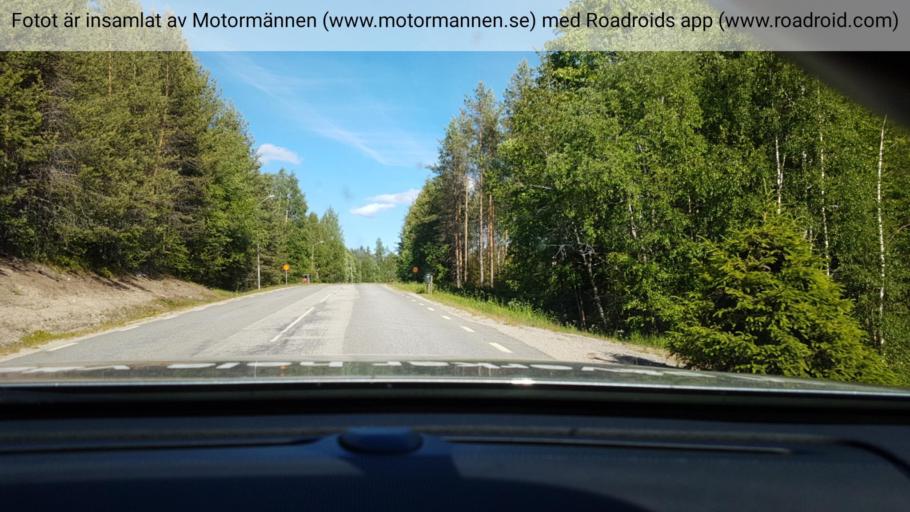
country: SE
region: Vaesterbotten
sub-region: Lycksele Kommun
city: Lycksele
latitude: 64.8170
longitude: 18.8775
